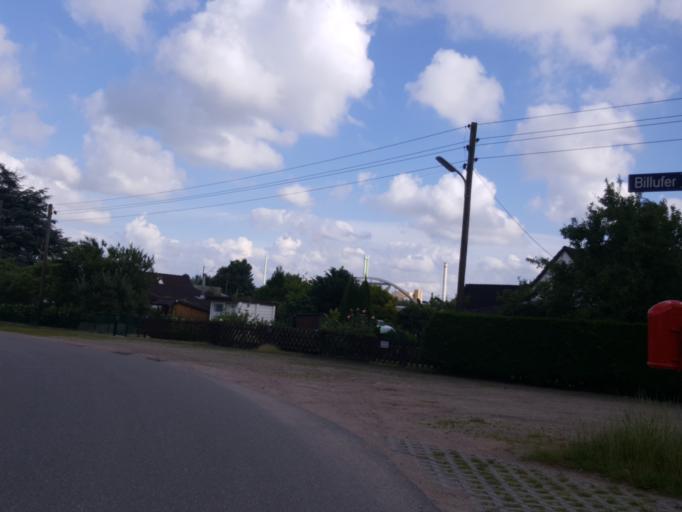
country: DE
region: Hamburg
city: Rothenburgsort
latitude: 53.5394
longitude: 10.0692
